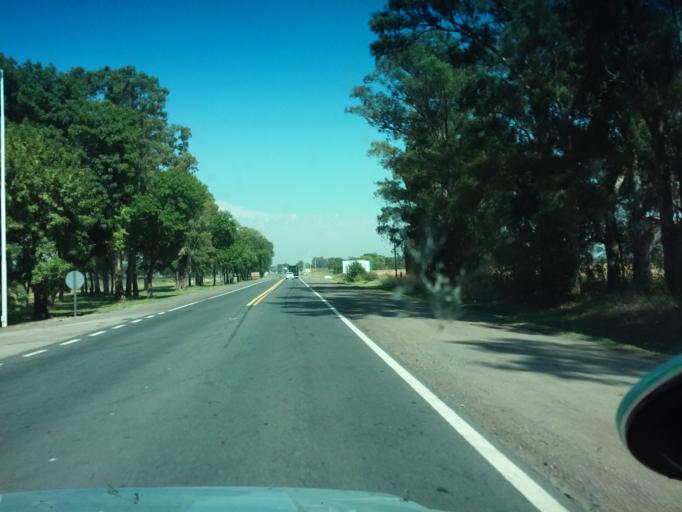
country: AR
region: Buenos Aires
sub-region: Partido de Nueve de Julio
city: Nueve de Julio
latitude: -35.4888
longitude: -60.8897
